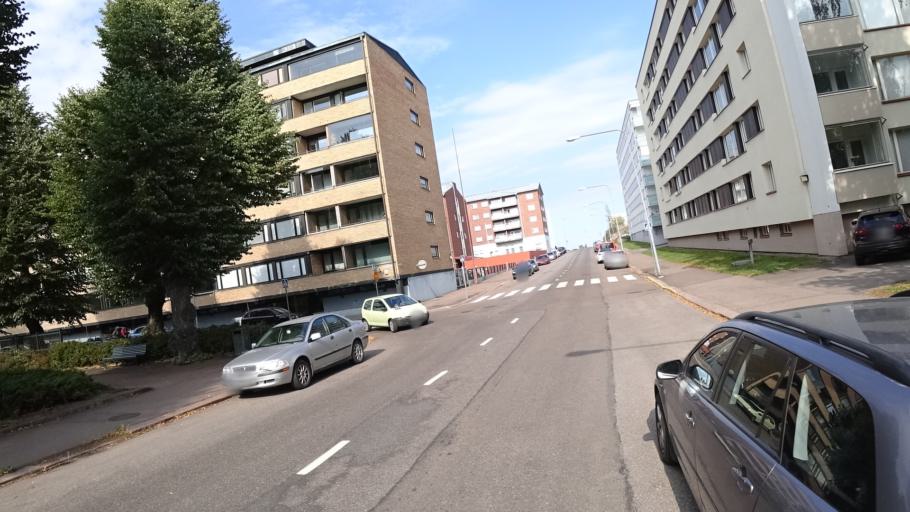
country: FI
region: Kymenlaakso
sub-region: Kotka-Hamina
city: Kotka
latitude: 60.4675
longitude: 26.9482
